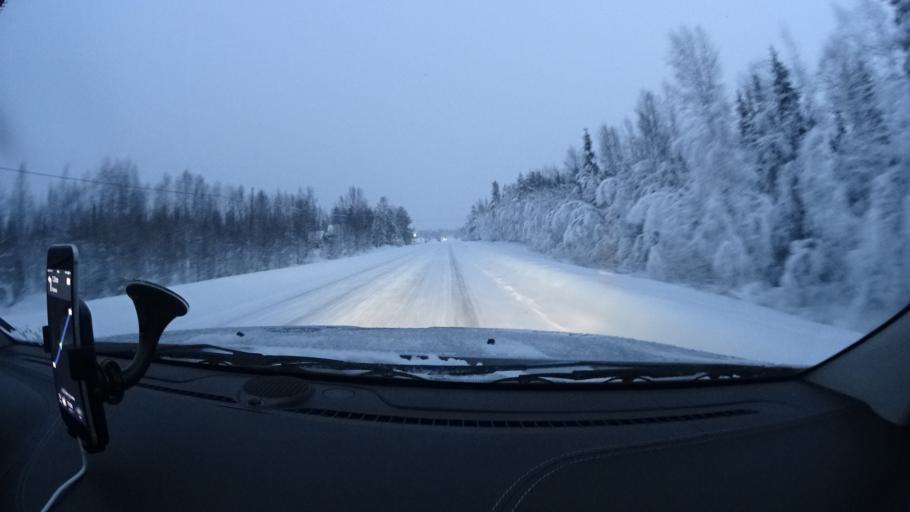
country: FI
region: Lapland
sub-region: Tunturi-Lappi
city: Kittilae
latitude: 67.6654
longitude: 24.8575
